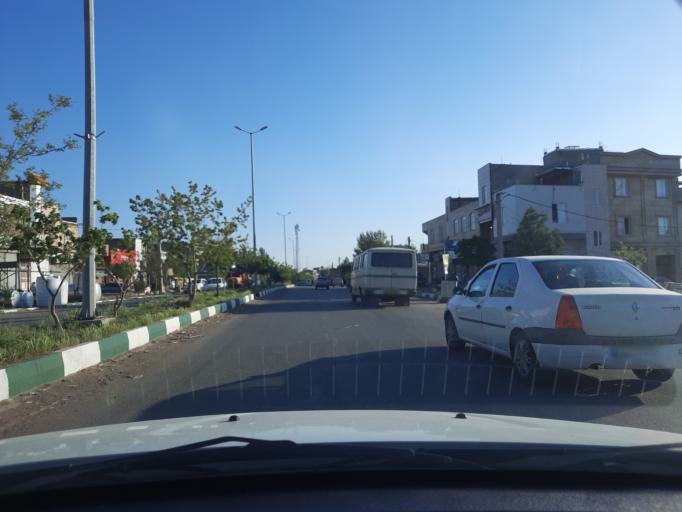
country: IR
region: Qazvin
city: Alvand
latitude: 36.2790
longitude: 50.1272
